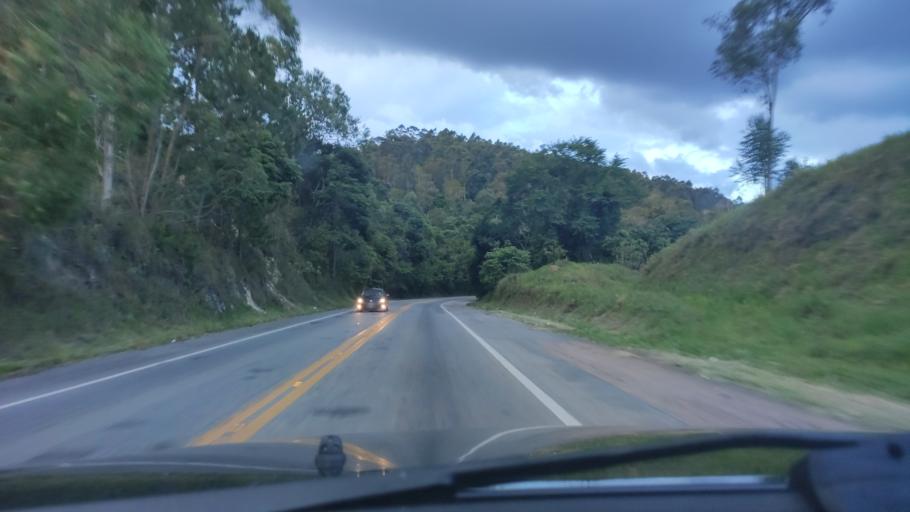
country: BR
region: Sao Paulo
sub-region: Braganca Paulista
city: Braganca Paulista
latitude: -22.8238
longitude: -46.5547
